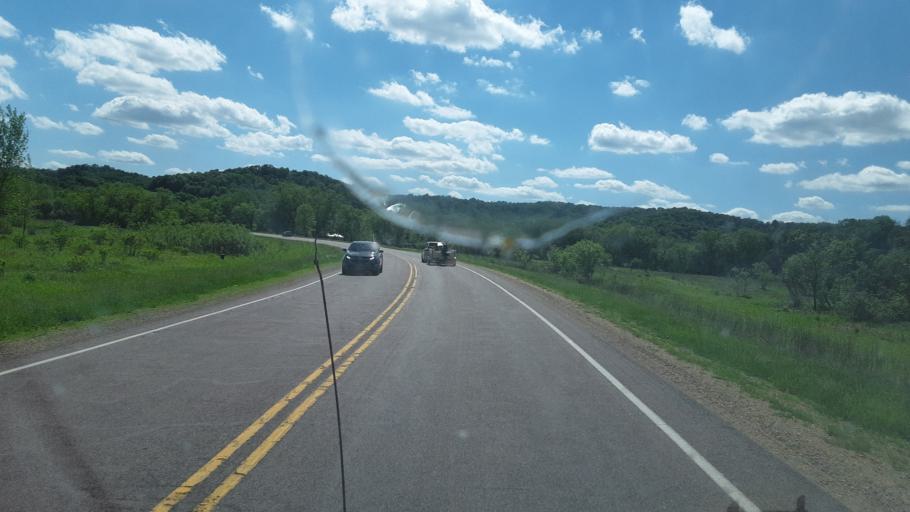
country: US
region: Wisconsin
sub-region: Richland County
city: Richland Center
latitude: 43.3751
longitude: -90.2635
